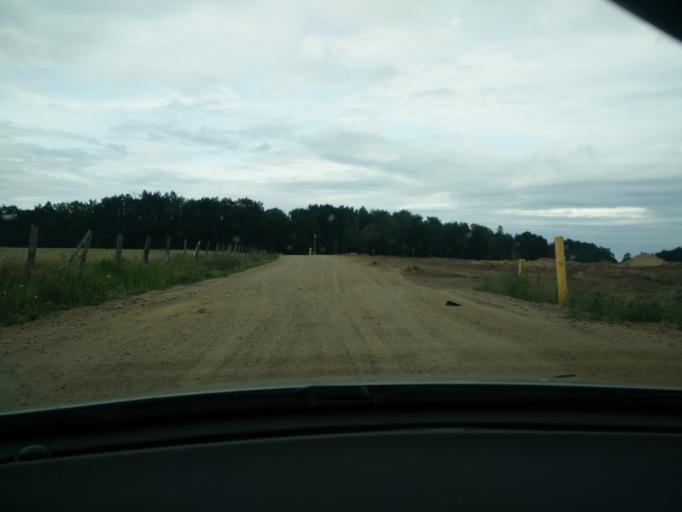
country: PL
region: Pomeranian Voivodeship
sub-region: Powiat pucki
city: Mrzezino
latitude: 54.6565
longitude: 18.4381
